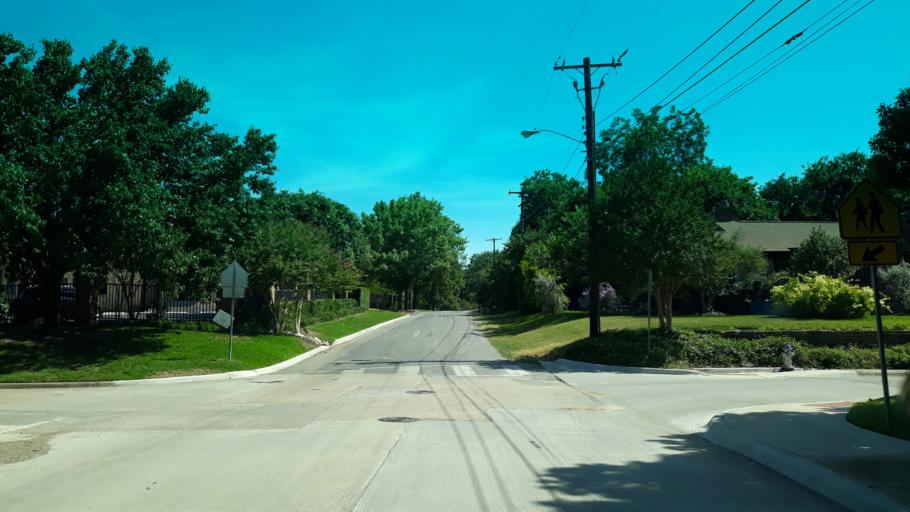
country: US
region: Texas
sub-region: Dallas County
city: Highland Park
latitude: 32.8239
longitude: -96.7499
